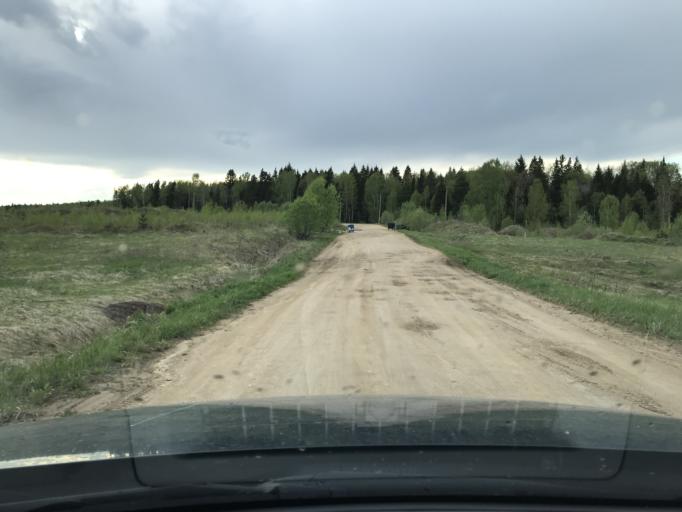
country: RU
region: Moskovskaya
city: Vereya
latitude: 55.3227
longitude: 36.3319
